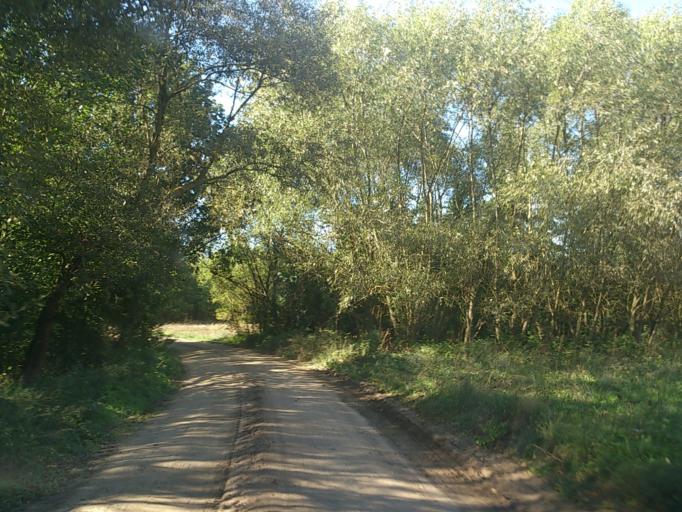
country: PL
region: Kujawsko-Pomorskie
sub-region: Powiat golubsko-dobrzynski
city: Golub-Dobrzyn
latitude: 53.1239
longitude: 19.1197
